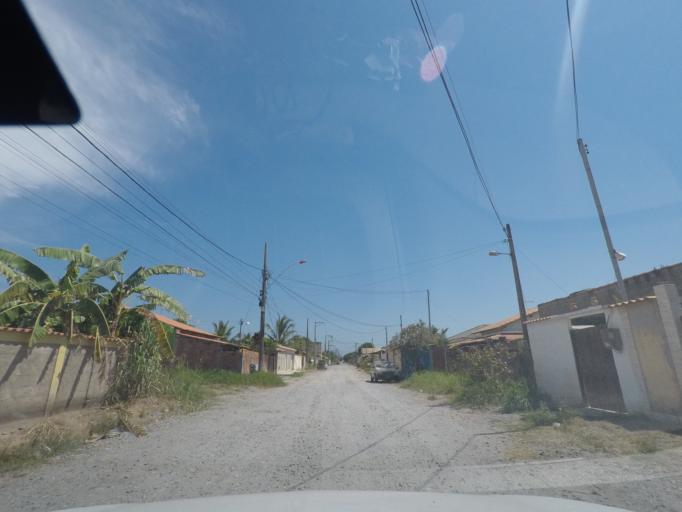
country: BR
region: Rio de Janeiro
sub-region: Marica
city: Marica
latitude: -22.9581
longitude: -42.9595
